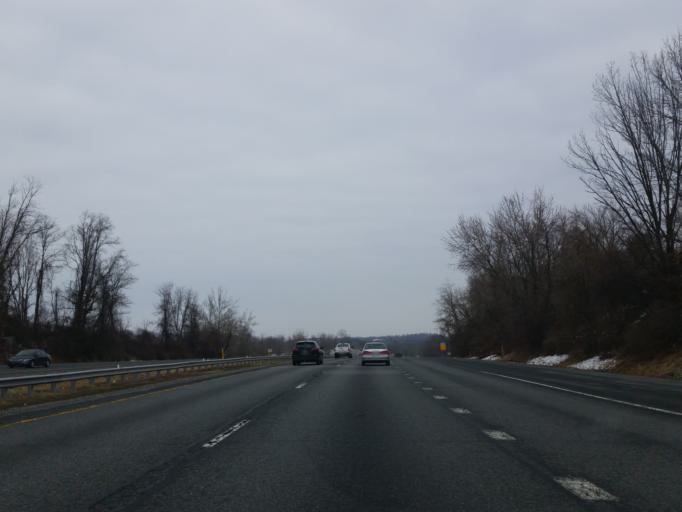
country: US
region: Maryland
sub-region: Baltimore County
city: Hunt Valley
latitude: 39.5002
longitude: -76.6674
